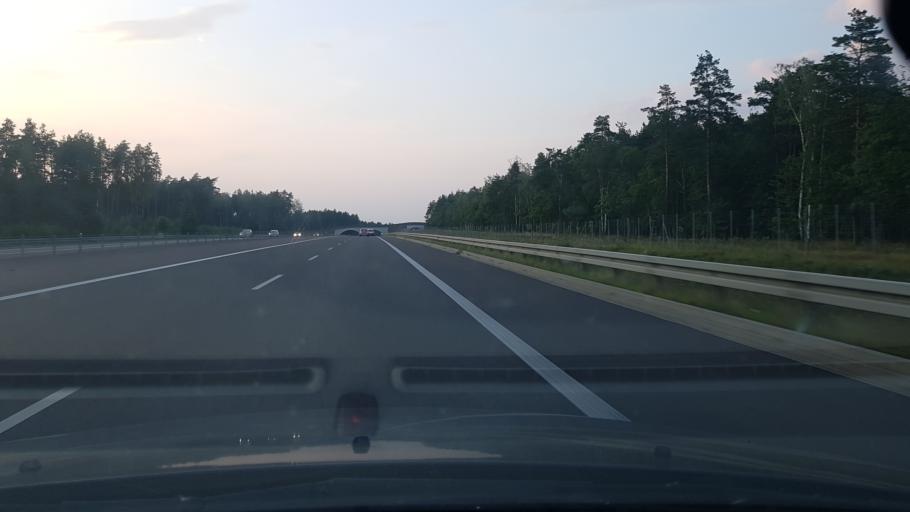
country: PL
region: Masovian Voivodeship
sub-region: Powiat mlawski
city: Wieczfnia Koscielna
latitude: 53.2468
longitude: 20.4244
